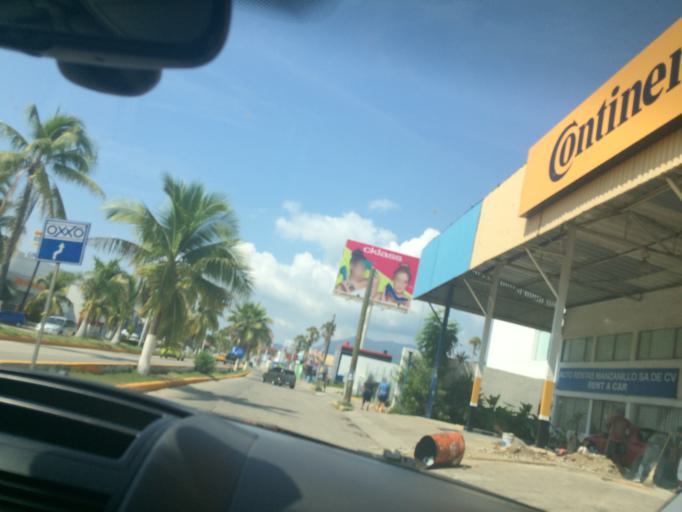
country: MX
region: Colima
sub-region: Manzanillo
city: Manzanillo
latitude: 19.1026
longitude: -104.3279
